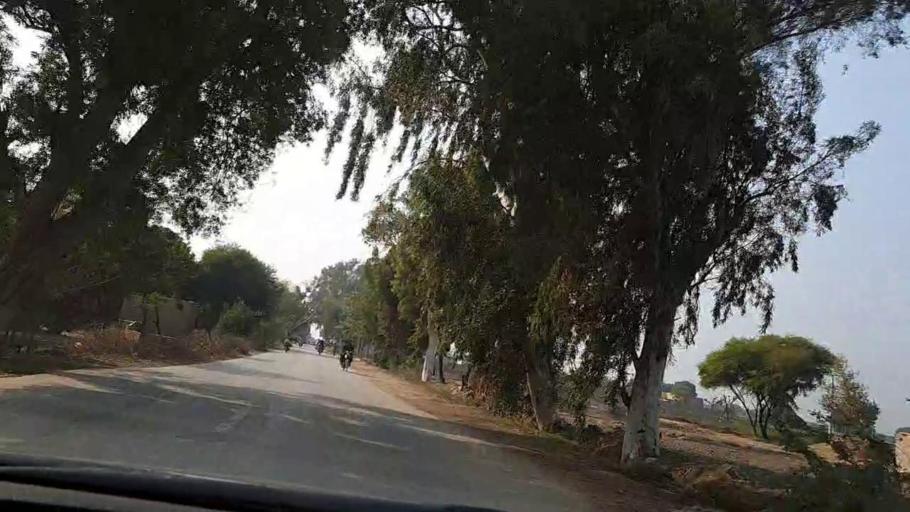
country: PK
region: Sindh
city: Sakrand
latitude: 26.1321
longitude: 68.2219
